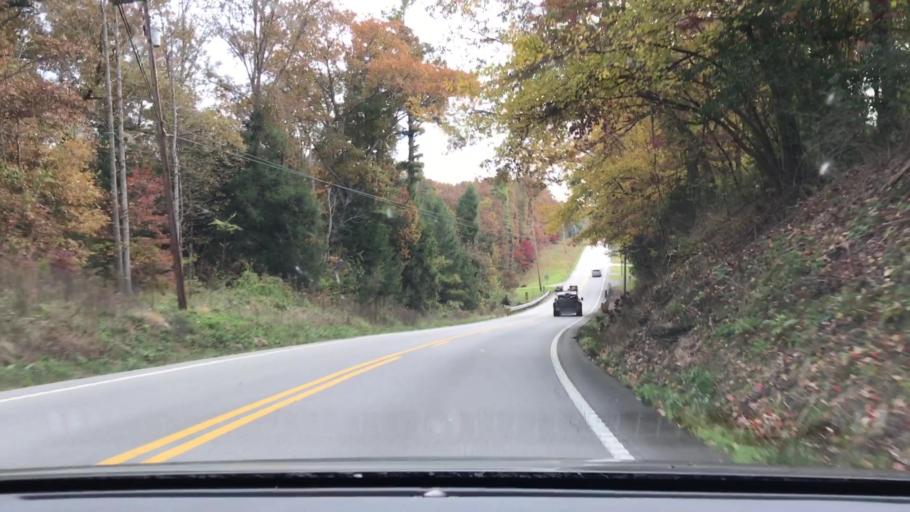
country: US
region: Tennessee
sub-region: Fentress County
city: Jamestown
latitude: 36.3748
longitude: -84.7787
